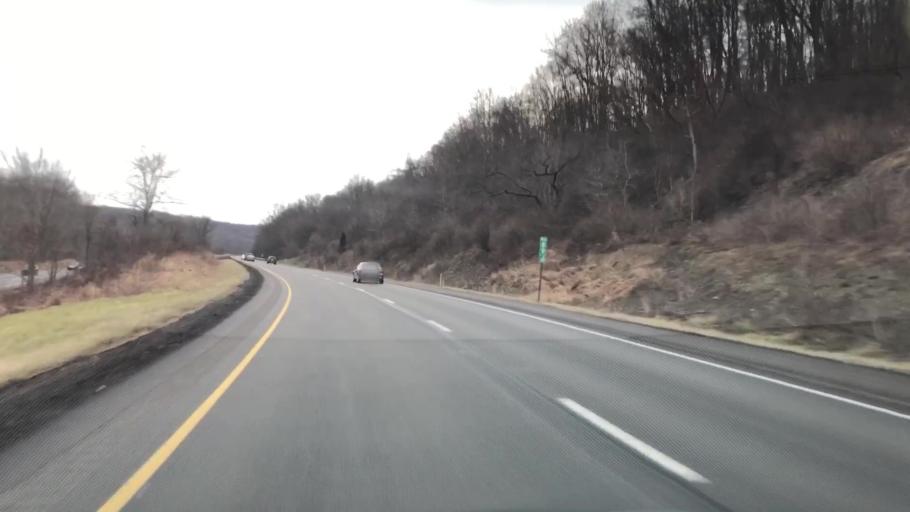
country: US
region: Pennsylvania
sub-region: Butler County
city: Zelienople
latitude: 40.8339
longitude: -80.1053
